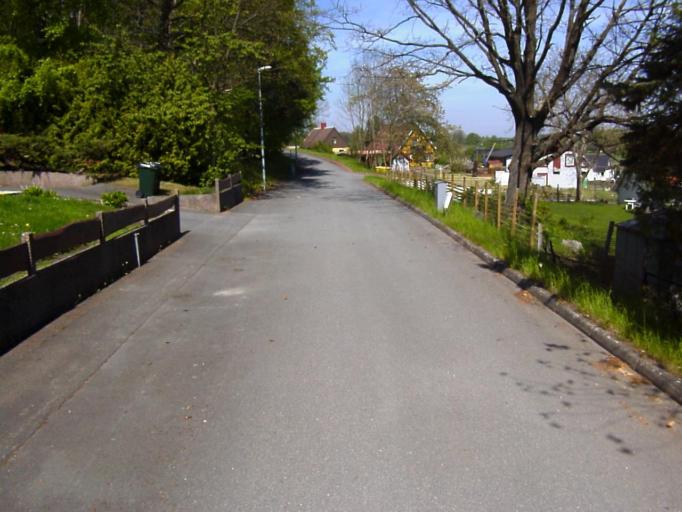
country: SE
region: Skane
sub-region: Kristianstads Kommun
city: Degeberga
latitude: 55.8861
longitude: 14.0140
